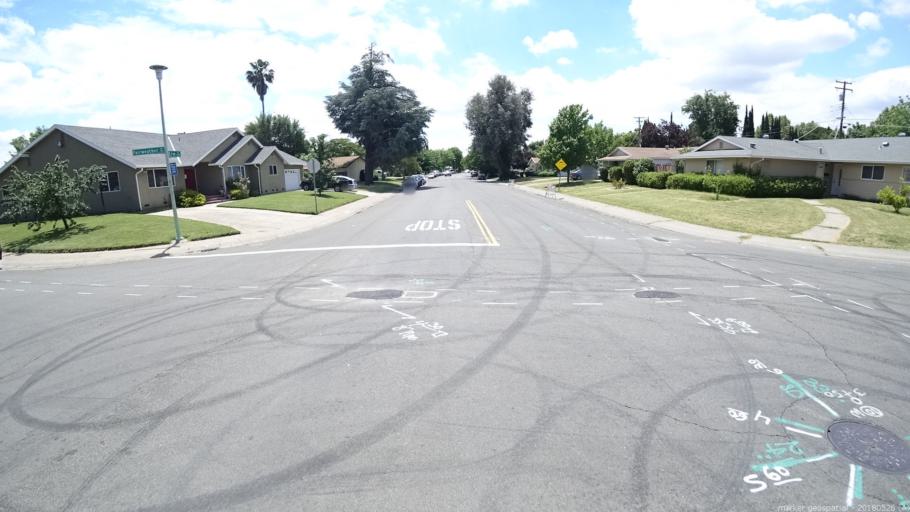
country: US
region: California
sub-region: Sacramento County
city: Sacramento
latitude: 38.6174
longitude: -121.4872
